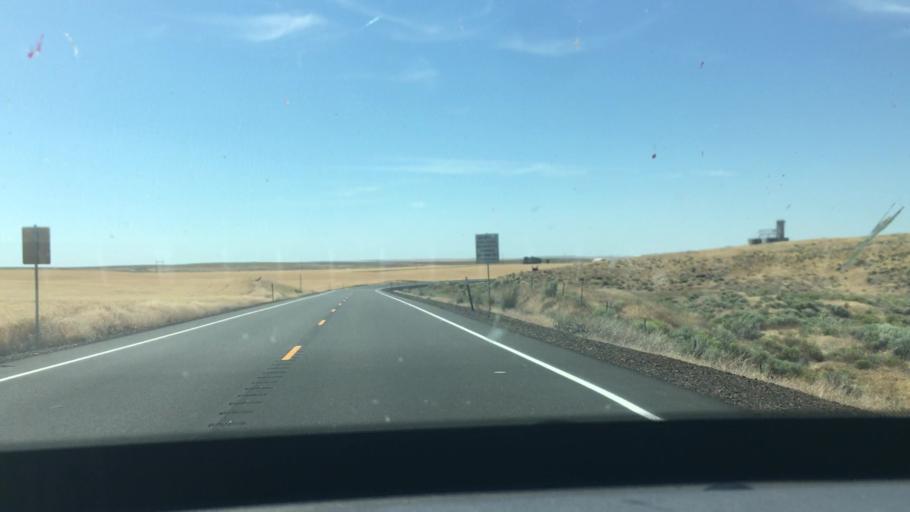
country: US
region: Oregon
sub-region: Sherman County
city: Moro
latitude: 45.3453
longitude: -120.7809
